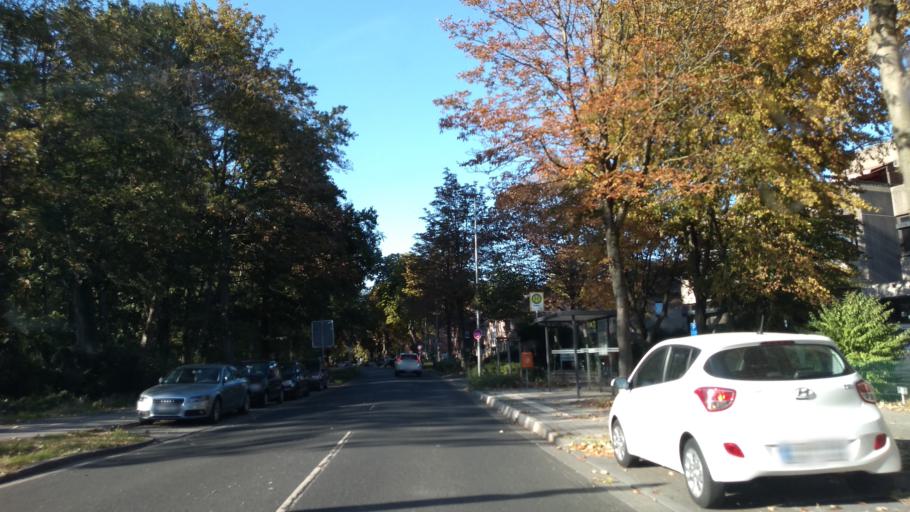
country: DE
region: North Rhine-Westphalia
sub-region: Regierungsbezirk Dusseldorf
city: Dinslaken
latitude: 51.5560
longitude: 6.7387
